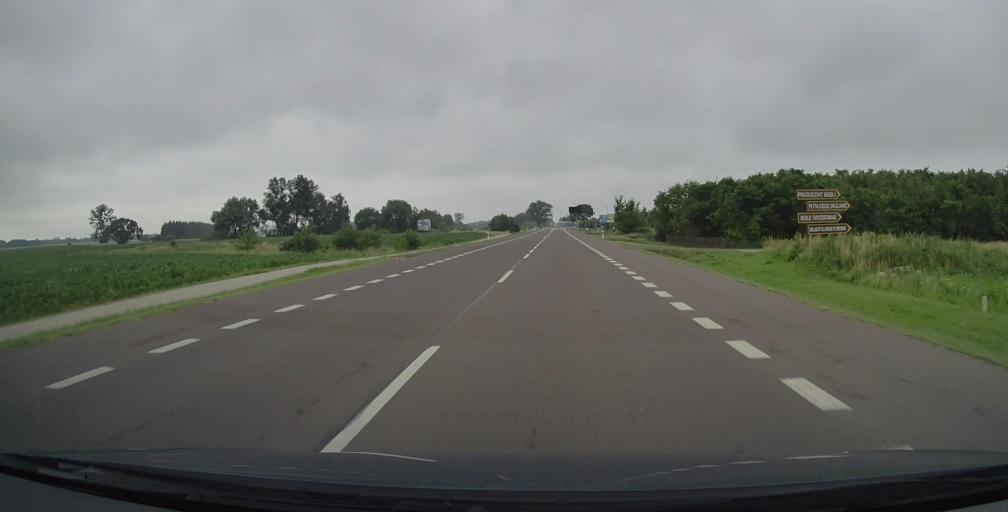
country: PL
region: Lublin Voivodeship
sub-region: Powiat bialski
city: Terespol
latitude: 52.0598
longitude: 23.5767
